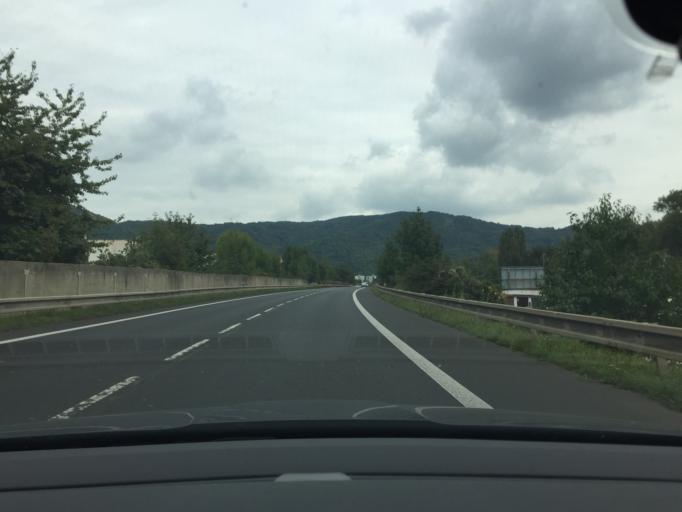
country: CZ
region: Ustecky
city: Velke Brezno
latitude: 50.6716
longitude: 14.1049
